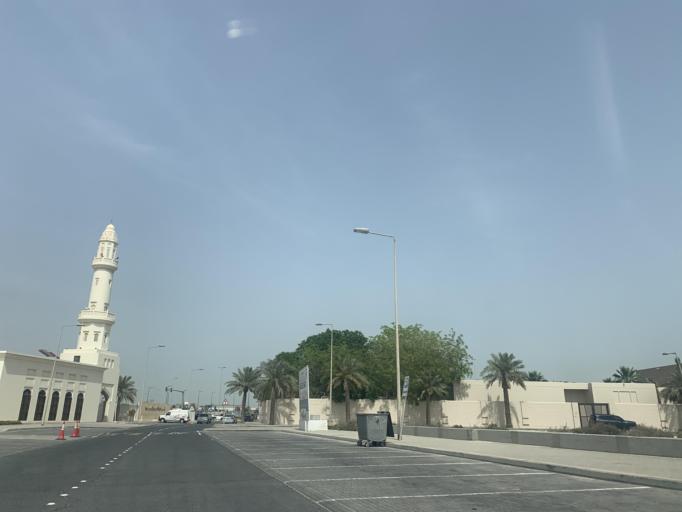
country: BH
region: Northern
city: Madinat `Isa
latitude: 26.1503
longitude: 50.5405
